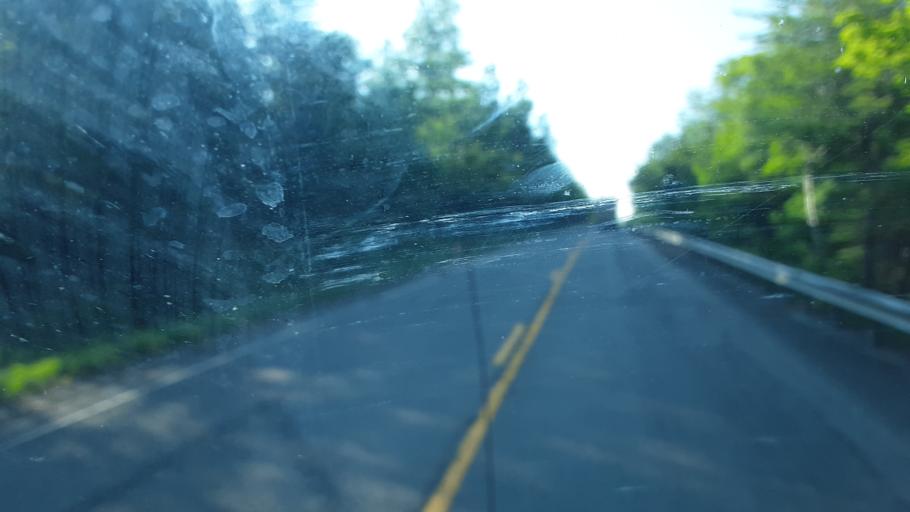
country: US
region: Maine
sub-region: Penobscot County
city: Patten
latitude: 46.2006
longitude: -68.2760
